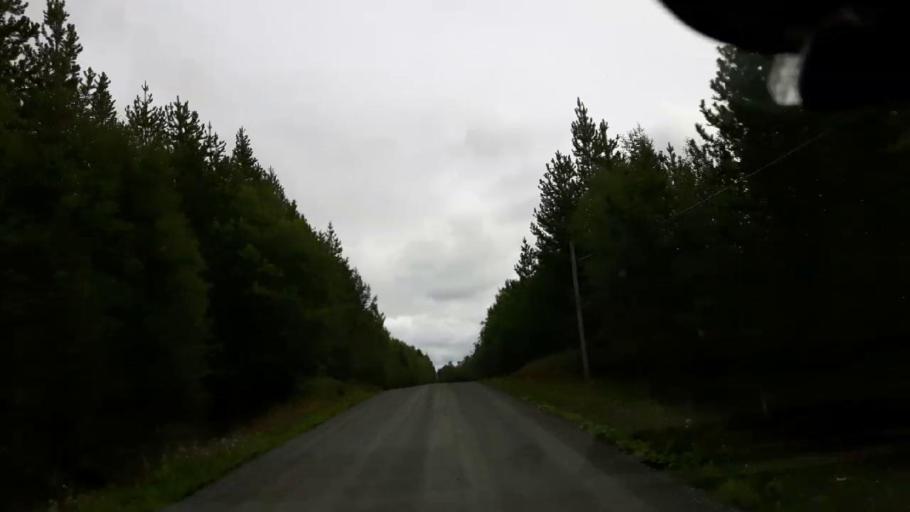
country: SE
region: Jaemtland
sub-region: Krokoms Kommun
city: Valla
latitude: 63.6874
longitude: 13.9005
